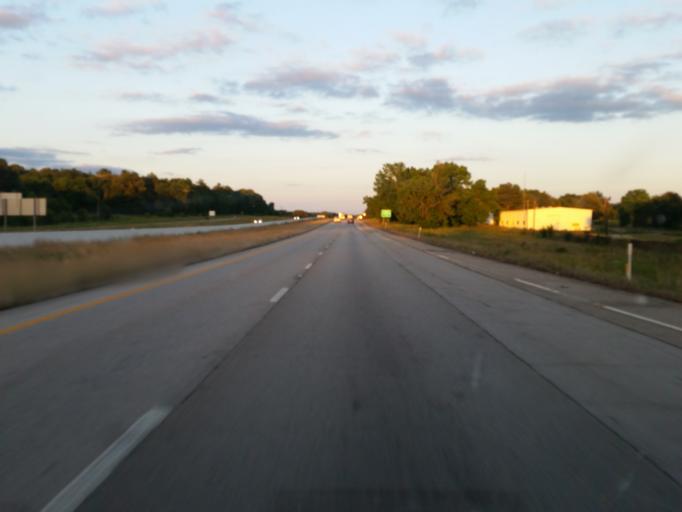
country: US
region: Texas
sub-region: Van Zandt County
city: Van
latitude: 32.4978
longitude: -95.5807
